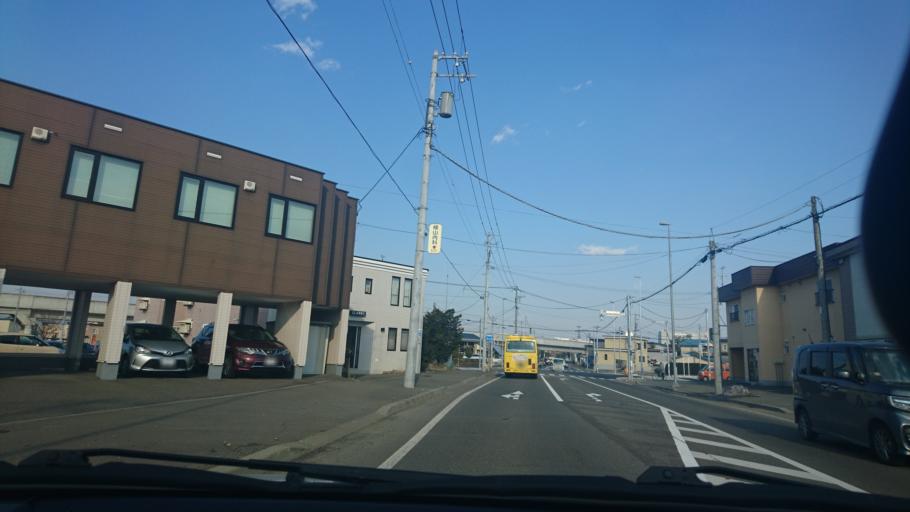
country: JP
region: Hokkaido
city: Obihiro
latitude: 42.9248
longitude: 143.1849
